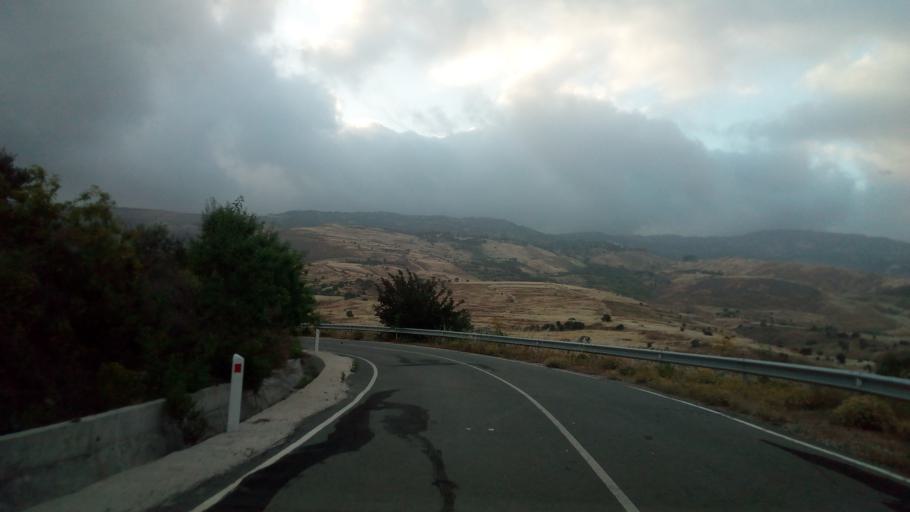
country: CY
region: Limassol
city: Pachna
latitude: 34.8643
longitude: 32.6442
